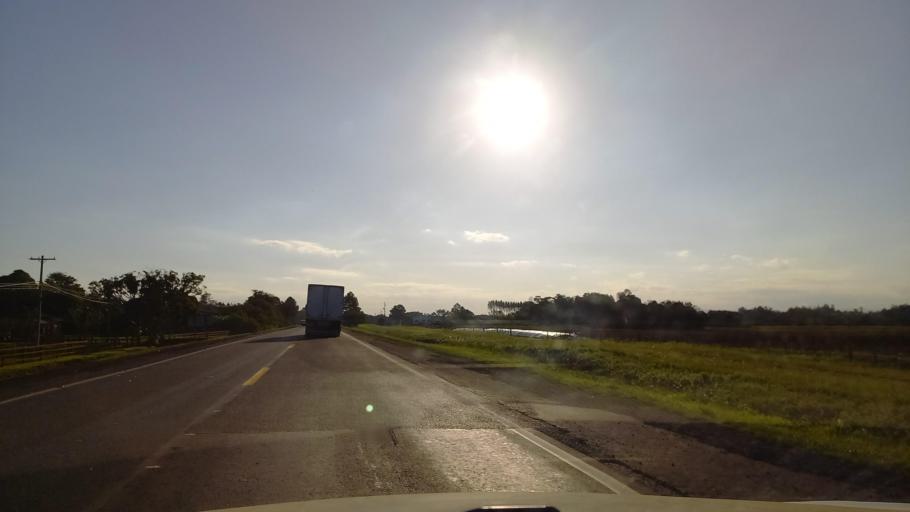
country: BR
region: Rio Grande do Sul
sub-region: Venancio Aires
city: Venancio Aires
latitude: -29.6621
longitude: -52.0653
